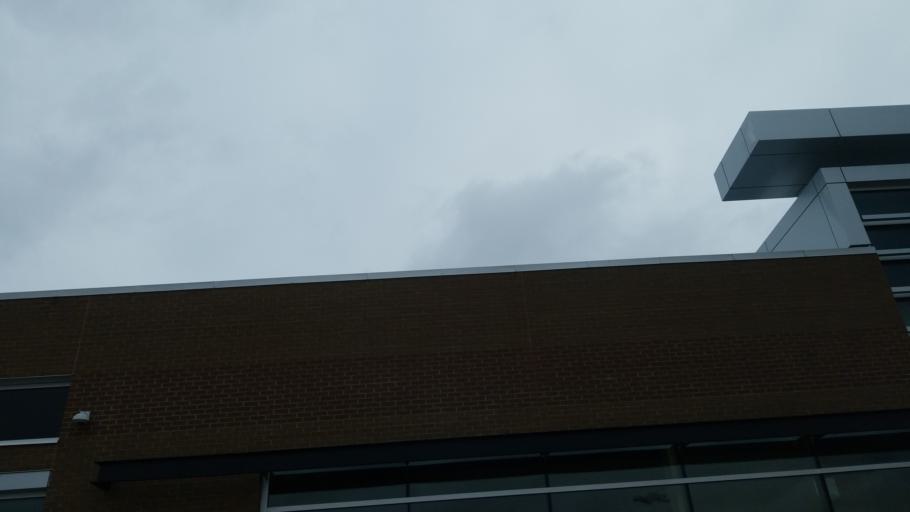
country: CA
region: Alberta
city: Sherwood Park
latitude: 53.5294
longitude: -113.2941
